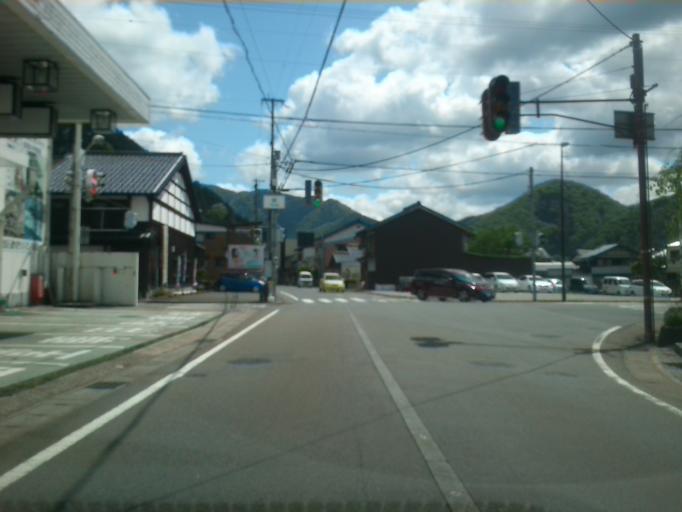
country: JP
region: Hyogo
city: Toyooka
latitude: 35.4628
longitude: 134.8713
